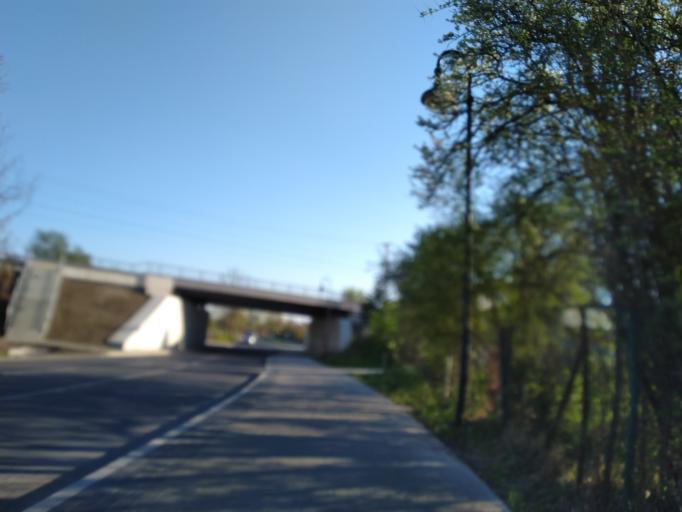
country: DE
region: Brandenburg
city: Bernau bei Berlin
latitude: 52.6673
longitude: 13.5583
